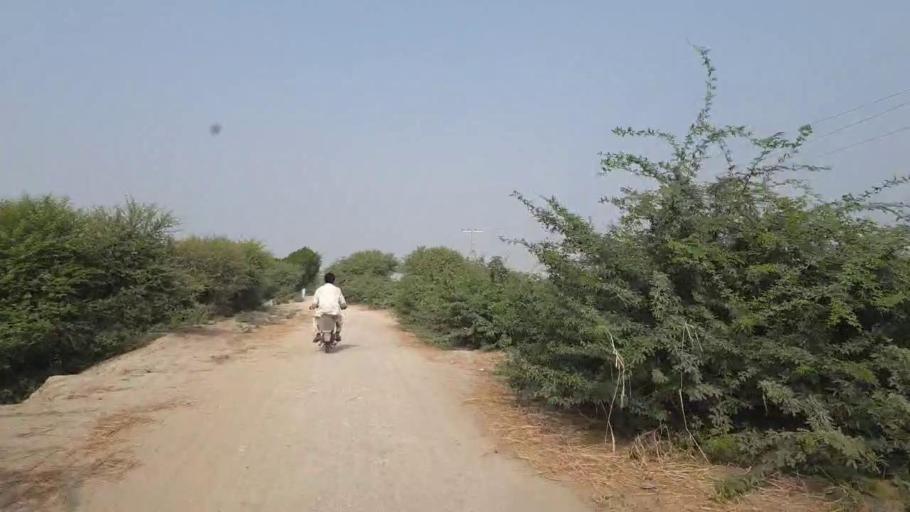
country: PK
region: Sindh
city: Kario
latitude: 24.9273
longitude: 68.6010
